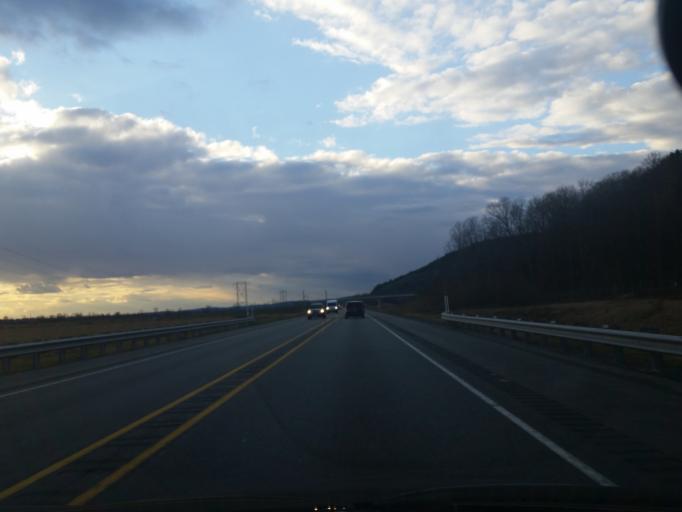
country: CA
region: Ontario
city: Hawkesbury
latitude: 45.6525
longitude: -74.7957
